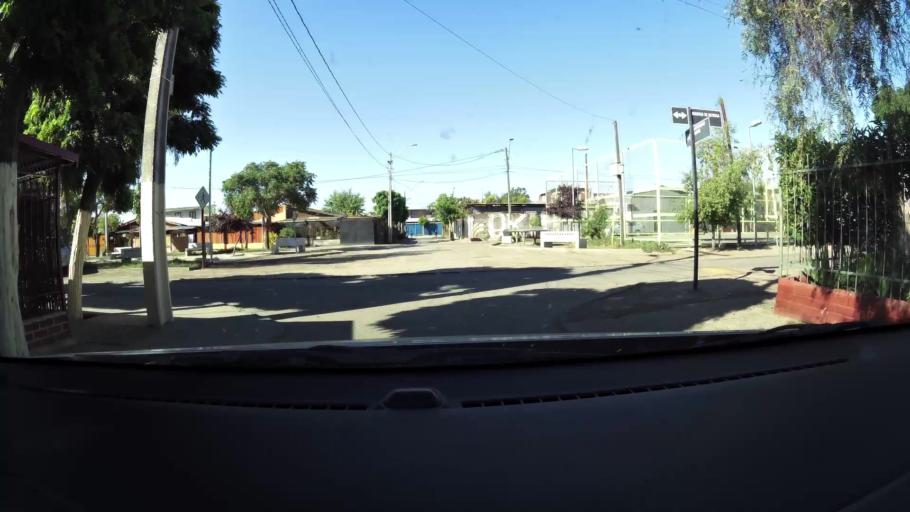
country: CL
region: Santiago Metropolitan
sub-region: Provincia de Maipo
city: San Bernardo
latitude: -33.5900
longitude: -70.6841
